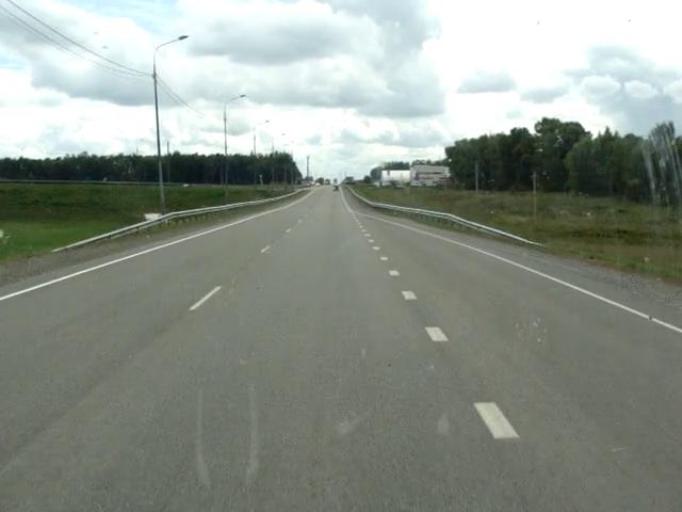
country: RU
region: Altai Krai
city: Zarya
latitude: 52.5785
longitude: 85.1776
